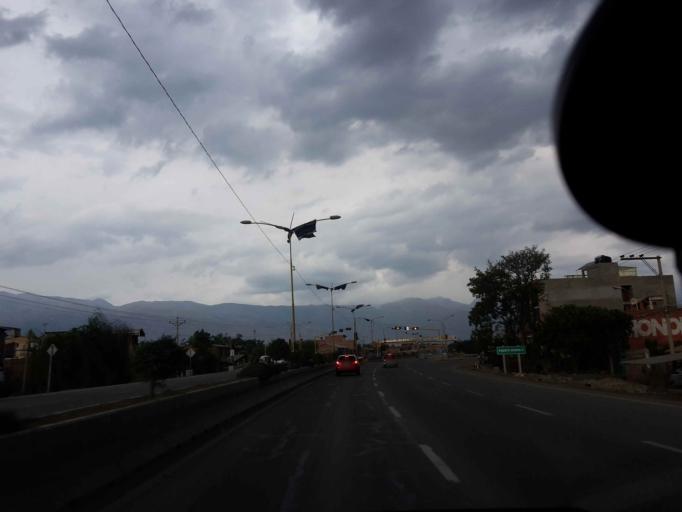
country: BO
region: Cochabamba
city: Sipe Sipe
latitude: -17.3994
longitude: -66.3273
